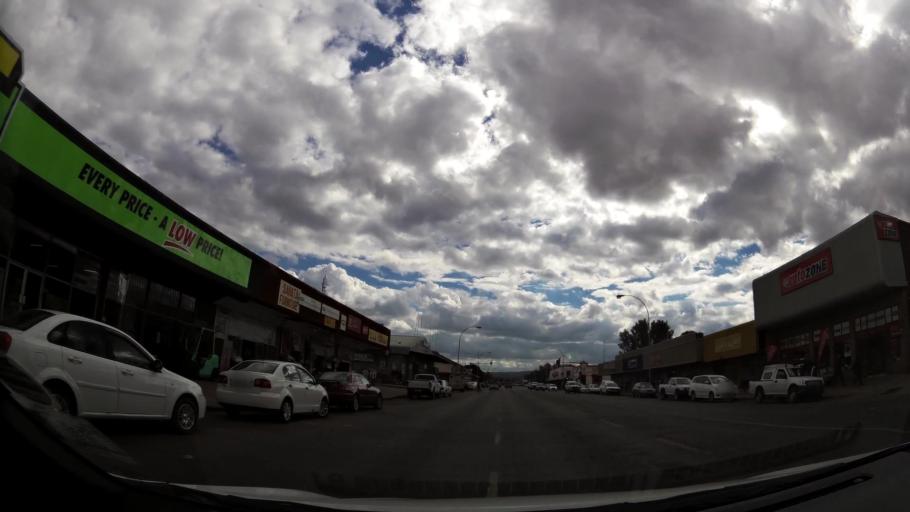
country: ZA
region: Limpopo
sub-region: Waterberg District Municipality
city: Modimolle
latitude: -24.7054
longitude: 28.4107
